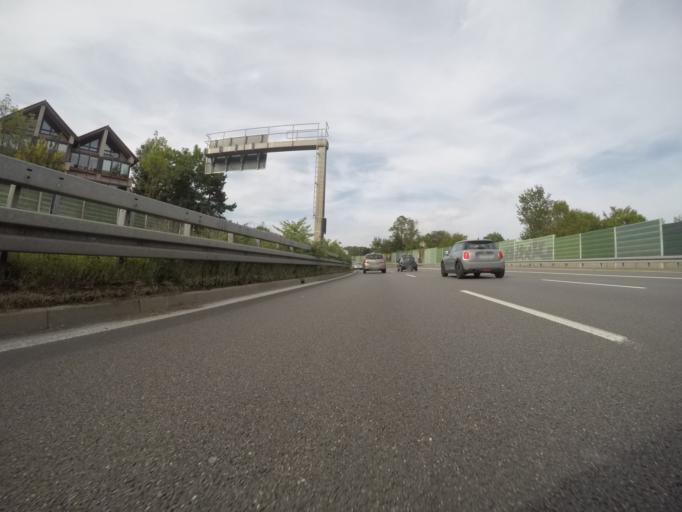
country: DE
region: Baden-Wuerttemberg
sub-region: Regierungsbezirk Stuttgart
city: Gerlingen
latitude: 48.7449
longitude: 9.1122
